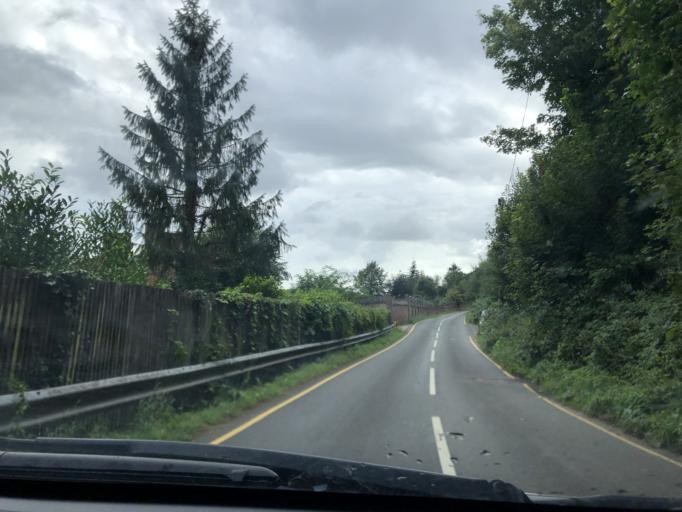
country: GB
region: England
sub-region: Kent
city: Westerham
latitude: 51.2453
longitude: 0.0830
